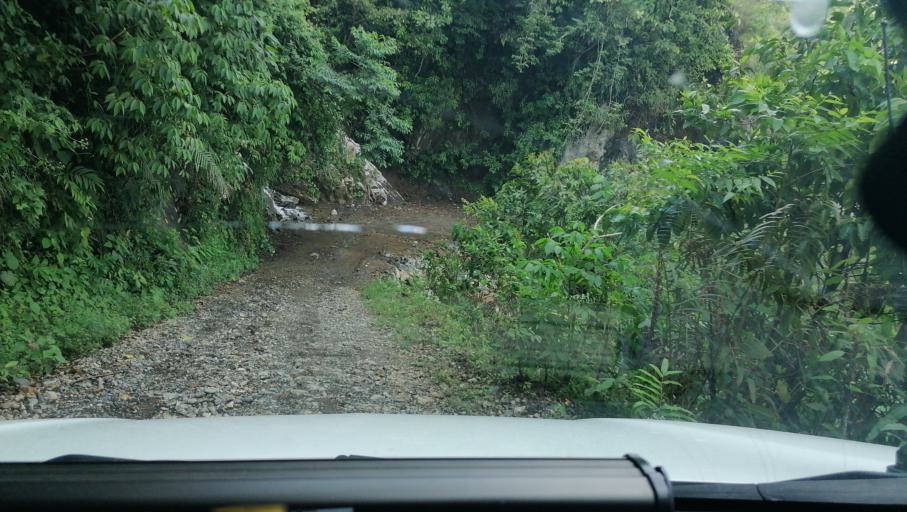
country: MX
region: Chiapas
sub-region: Tapilula
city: San Francisco Jacona
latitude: 17.3020
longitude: -93.1036
